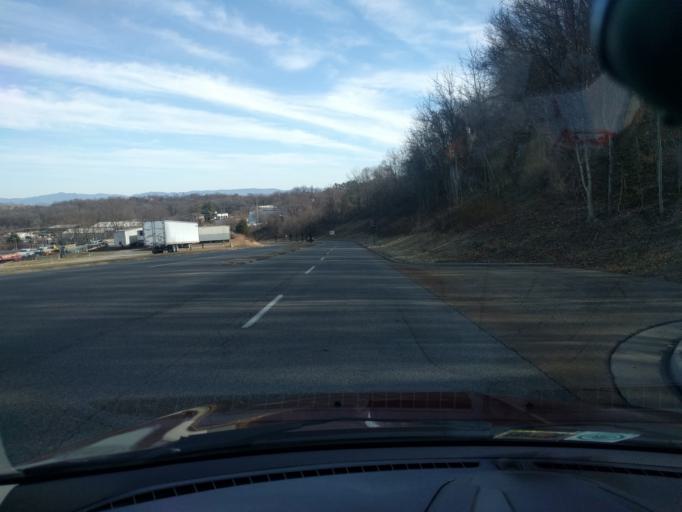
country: US
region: Virginia
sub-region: City of Staunton
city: Staunton
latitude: 38.1427
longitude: -79.0601
